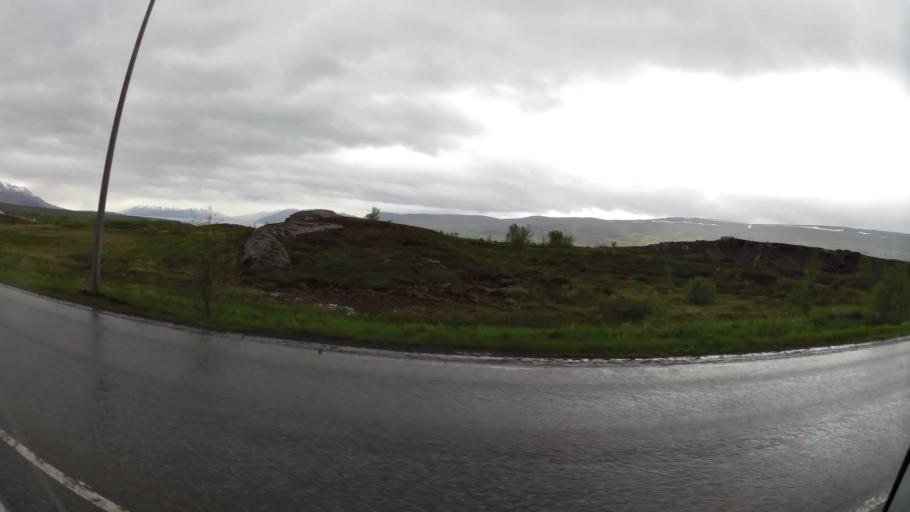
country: IS
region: Northeast
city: Akureyri
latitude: 65.7014
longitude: -18.1474
